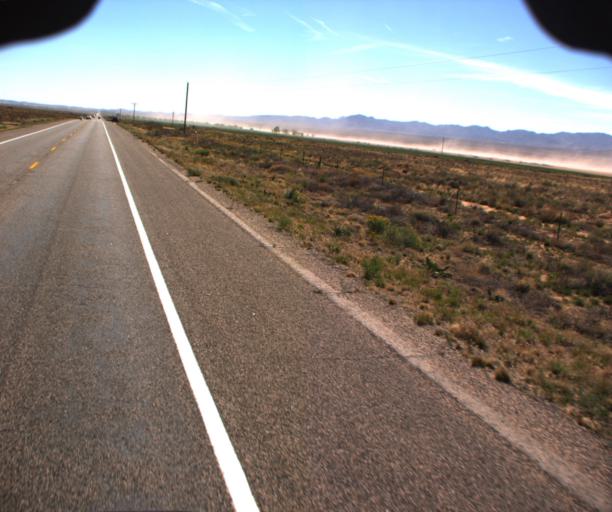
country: US
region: Arizona
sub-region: Mohave County
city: New Kingman-Butler
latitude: 35.3595
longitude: -113.8746
